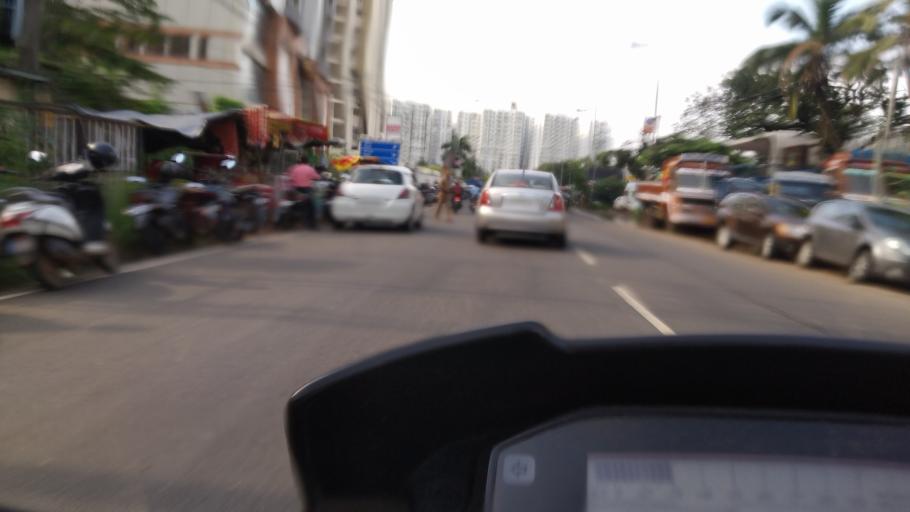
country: IN
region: Kerala
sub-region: Ernakulam
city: Cochin
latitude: 9.9891
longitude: 76.2712
